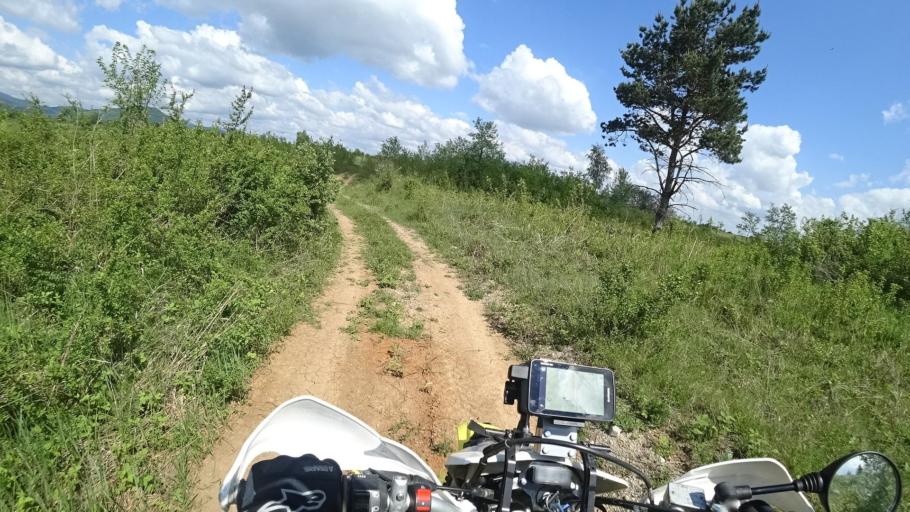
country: BA
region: Federation of Bosnia and Herzegovina
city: Izacic
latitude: 44.8697
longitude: 15.7564
